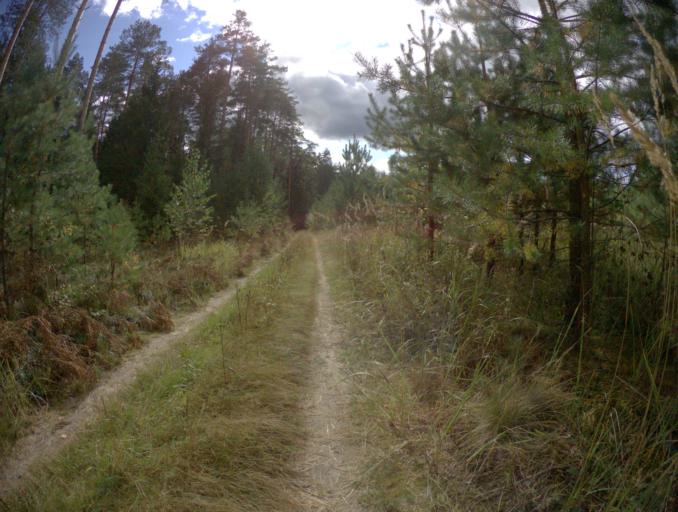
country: RU
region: Vladimir
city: Golovino
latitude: 55.9045
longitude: 40.4425
